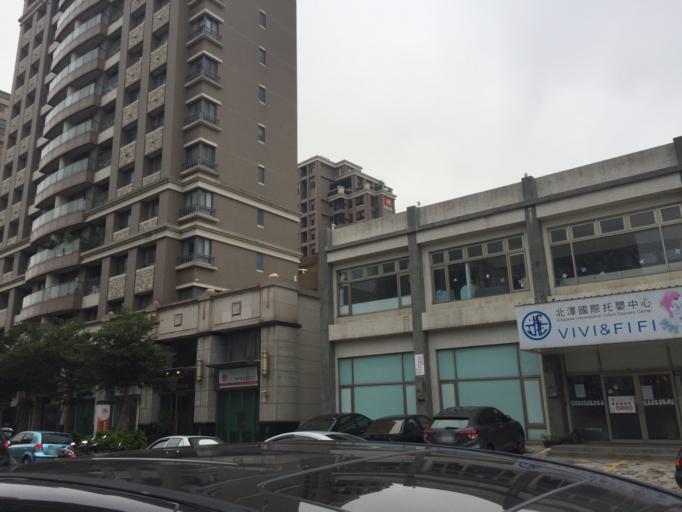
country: TW
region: Taiwan
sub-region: Hsinchu
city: Zhubei
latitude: 24.8200
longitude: 121.0221
